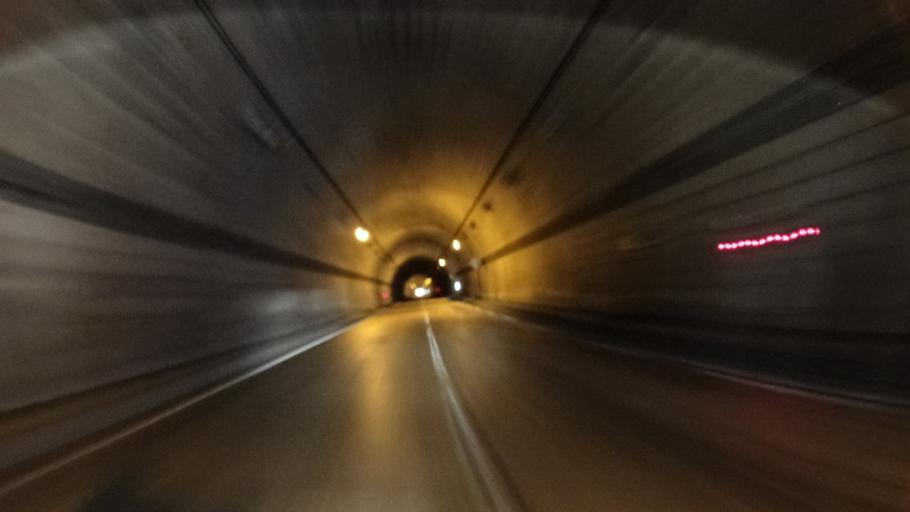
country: JP
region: Niigata
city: Shiozawa
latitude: 36.9834
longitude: 138.7767
